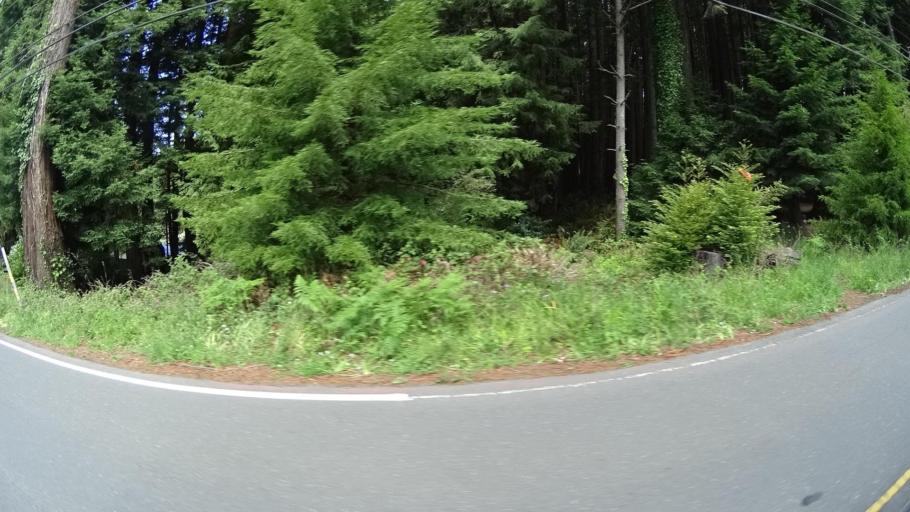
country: US
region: California
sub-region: Humboldt County
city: Arcata
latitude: 40.8684
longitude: -124.0704
